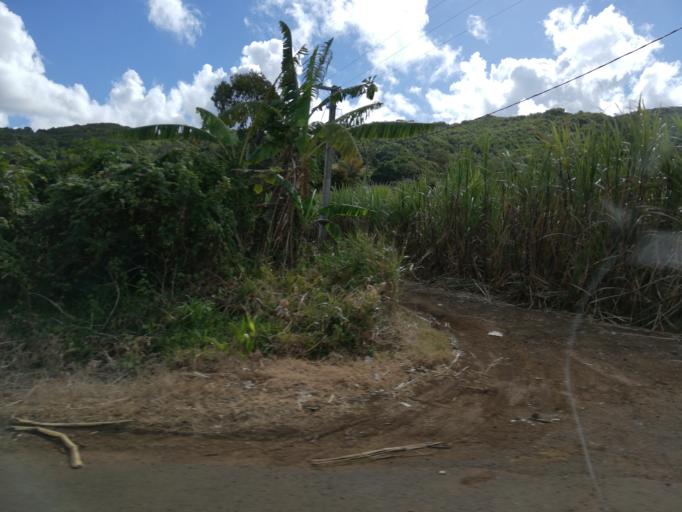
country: MU
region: Grand Port
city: Mahebourg
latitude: -20.3934
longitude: 57.6902
